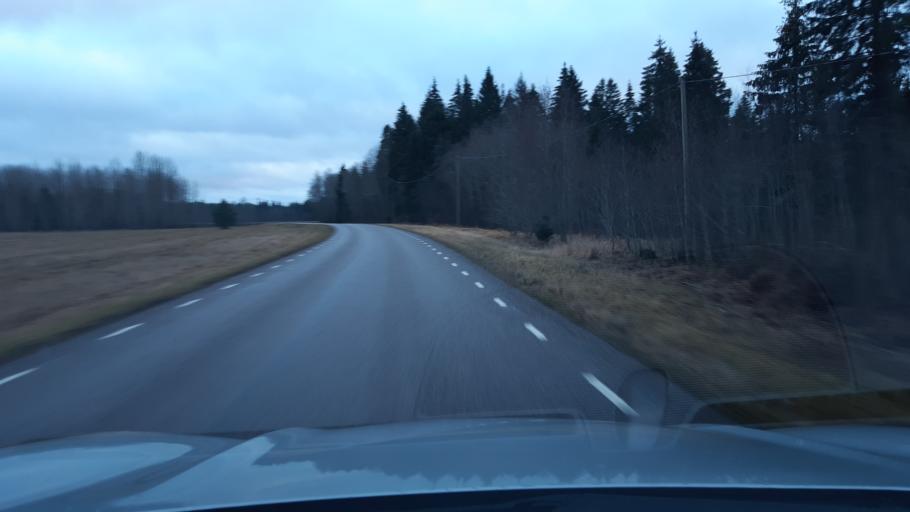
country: EE
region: Raplamaa
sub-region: Kohila vald
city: Kohila
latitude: 59.1444
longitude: 24.6534
